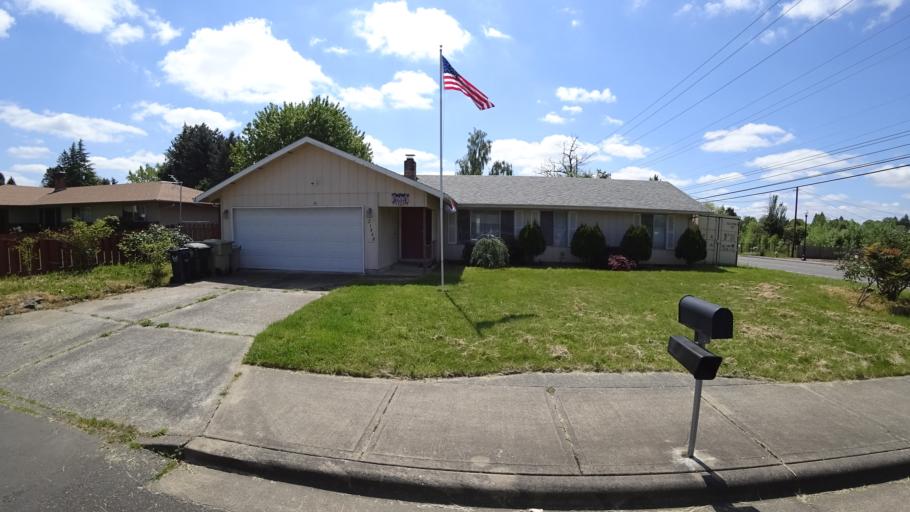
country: US
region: Oregon
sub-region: Washington County
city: Aloha
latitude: 45.5067
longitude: -122.9017
